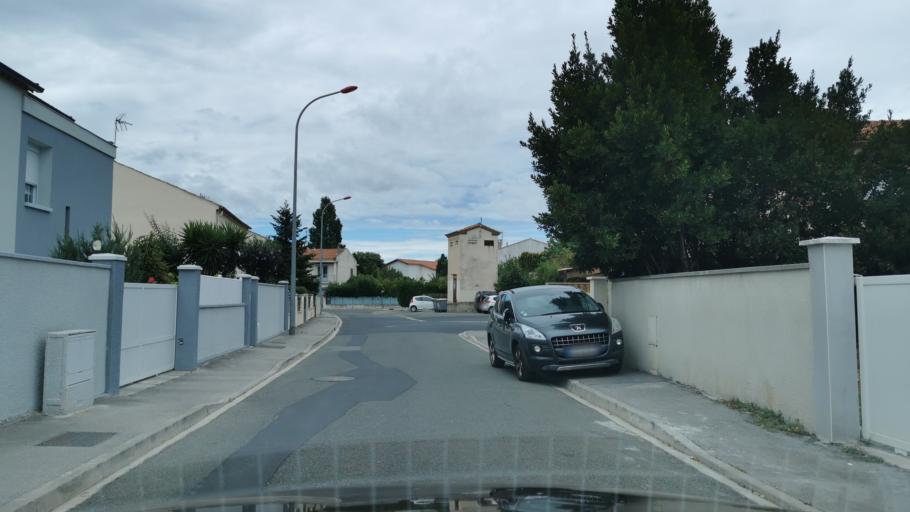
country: FR
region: Languedoc-Roussillon
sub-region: Departement de l'Aude
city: Narbonne
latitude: 43.1838
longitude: 3.0183
